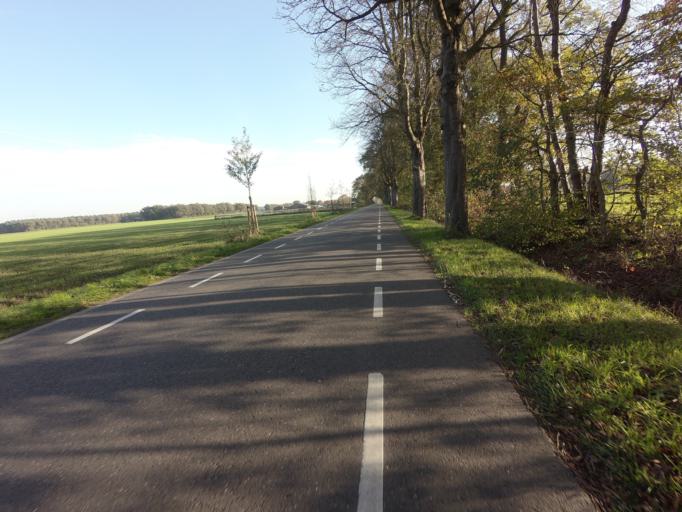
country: NL
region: Limburg
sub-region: Gemeente Roerdalen
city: Montfort
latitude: 51.1082
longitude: 5.9797
